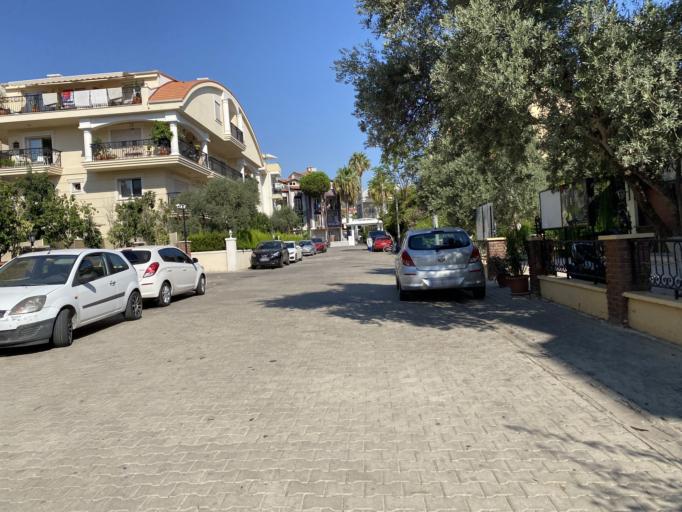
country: TR
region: Mugla
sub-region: Marmaris
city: Marmaris
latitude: 36.8447
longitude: 28.2523
